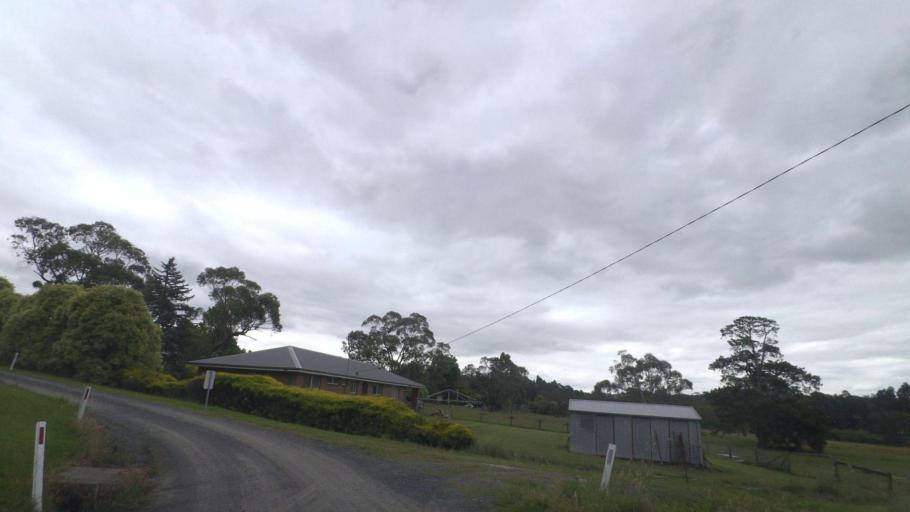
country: AU
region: Victoria
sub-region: Yarra Ranges
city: Mount Evelyn
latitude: -37.7758
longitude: 145.4242
